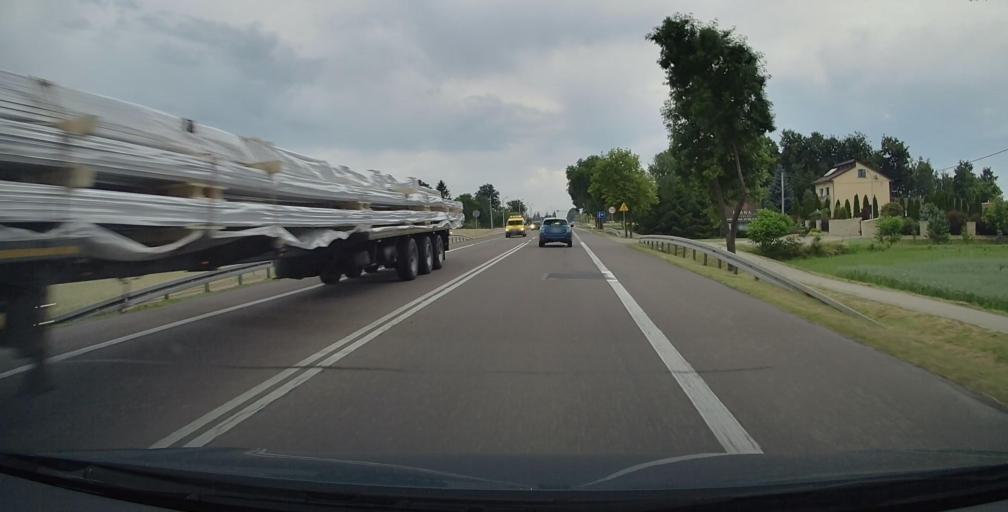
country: PL
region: Lublin Voivodeship
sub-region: Biala Podlaska
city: Biala Podlaska
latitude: 52.0345
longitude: 23.0441
